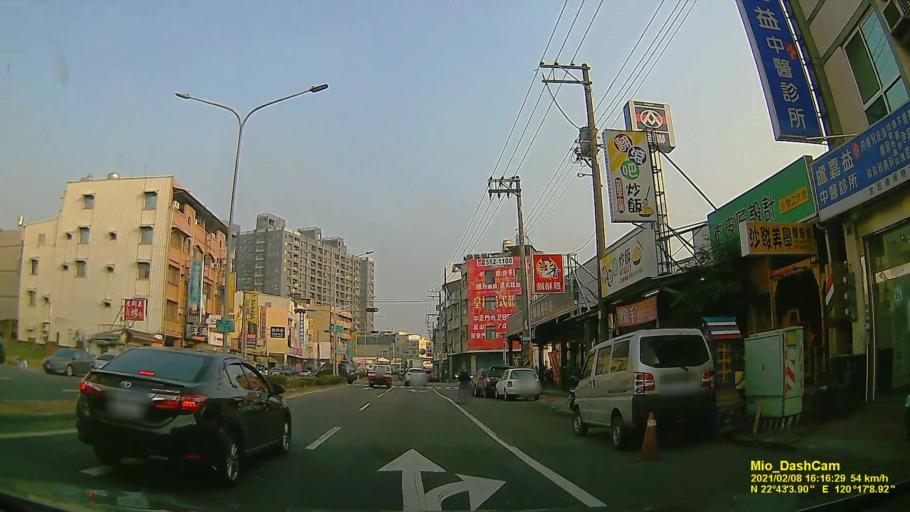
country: TW
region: Kaohsiung
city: Kaohsiung
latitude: 22.7177
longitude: 120.2859
